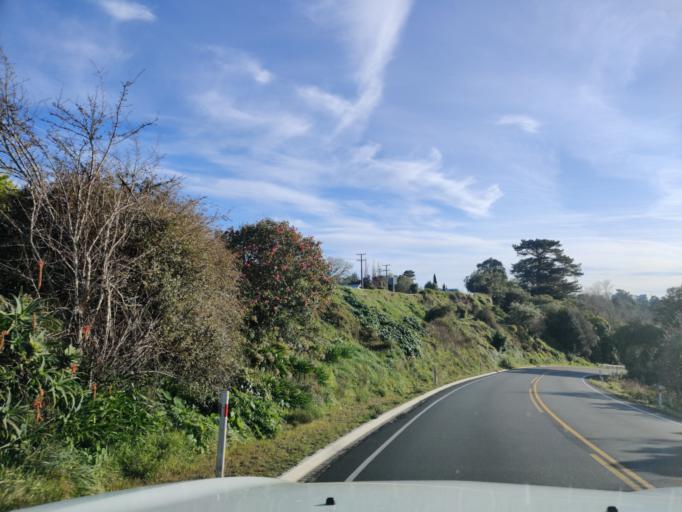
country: NZ
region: Manawatu-Wanganui
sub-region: Palmerston North City
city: Palmerston North
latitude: -40.2810
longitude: 175.7605
